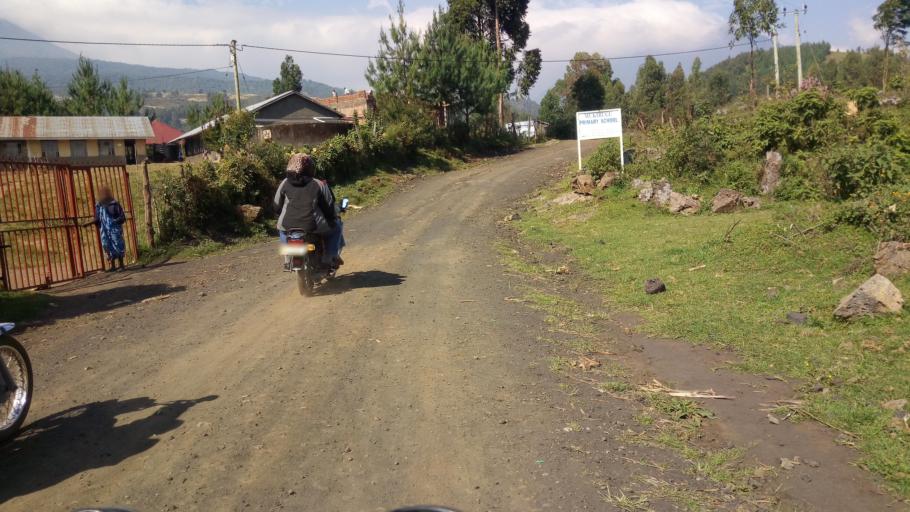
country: UG
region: Western Region
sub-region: Kisoro District
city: Kisoro
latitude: -1.3364
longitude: 29.6351
